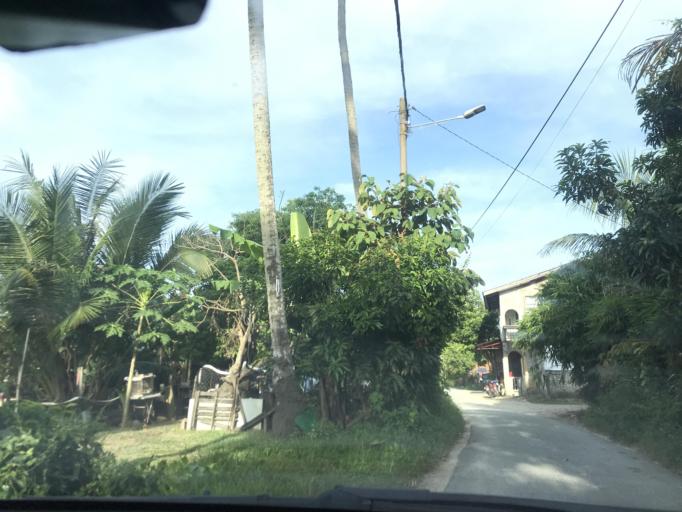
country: MY
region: Kelantan
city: Kota Bharu
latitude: 6.1273
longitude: 102.2227
